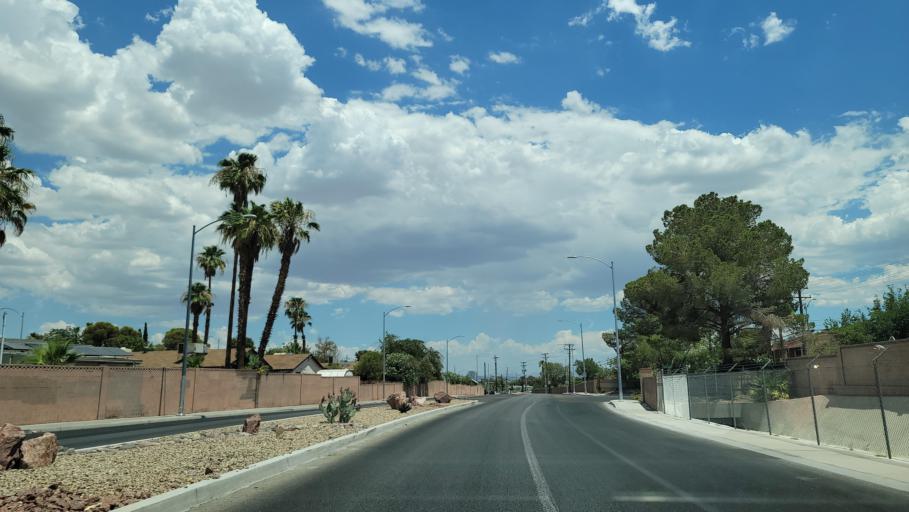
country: US
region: Nevada
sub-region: Clark County
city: Las Vegas
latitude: 36.1667
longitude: -115.1964
